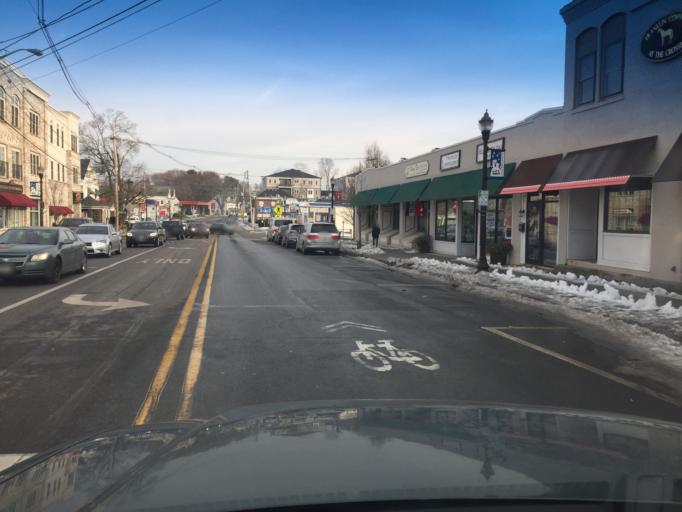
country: US
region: Massachusetts
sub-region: Norfolk County
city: Franklin
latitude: 42.0824
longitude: -71.3967
